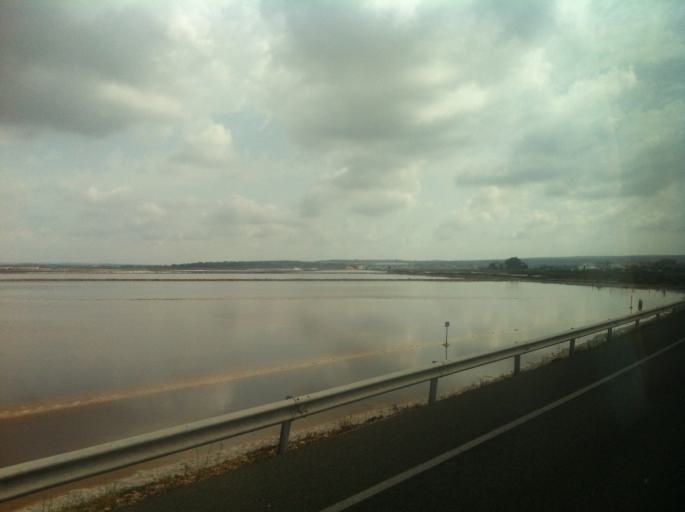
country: ES
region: Valencia
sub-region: Provincia de Alicante
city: Santa Pola
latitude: 38.1853
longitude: -0.6058
